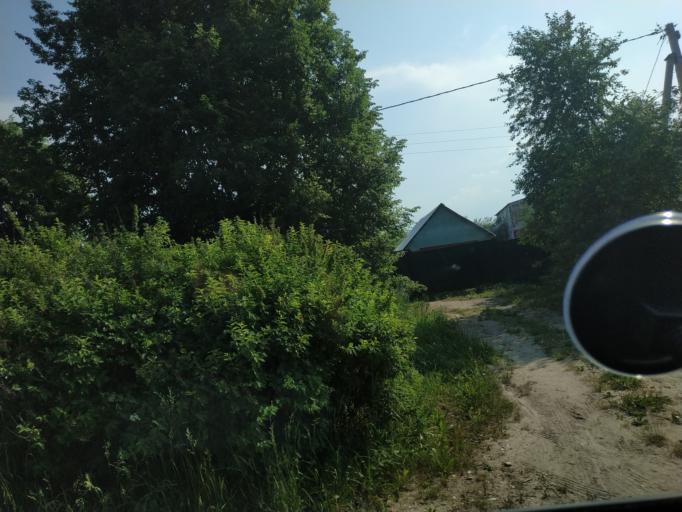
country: RU
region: Moskovskaya
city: Yakovlevskoye
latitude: 55.4256
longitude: 37.9538
